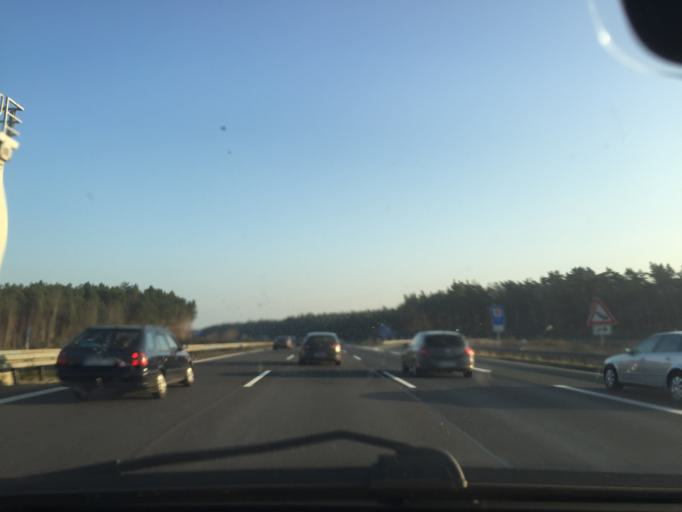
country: DE
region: Brandenburg
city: Michendorf
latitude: 52.2998
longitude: 13.0260
